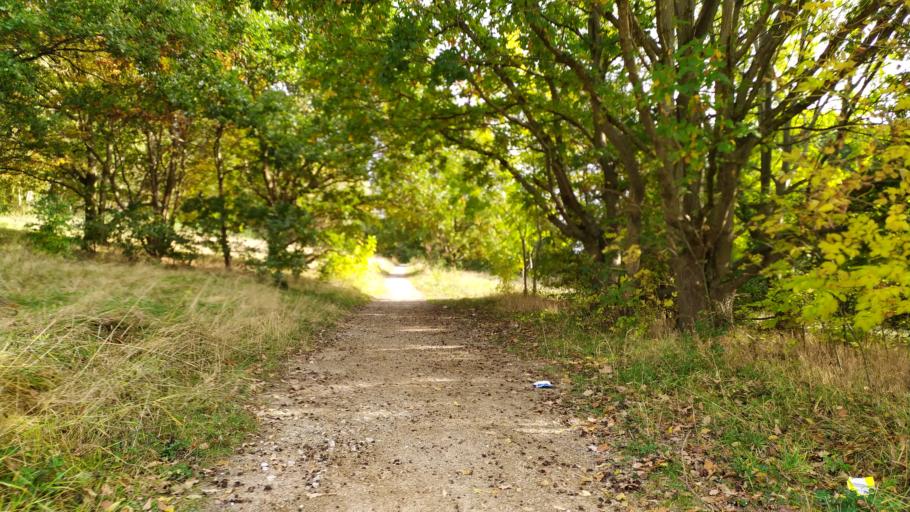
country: GB
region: England
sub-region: City and Borough of Leeds
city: Chapel Allerton
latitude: 53.8219
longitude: -1.5524
